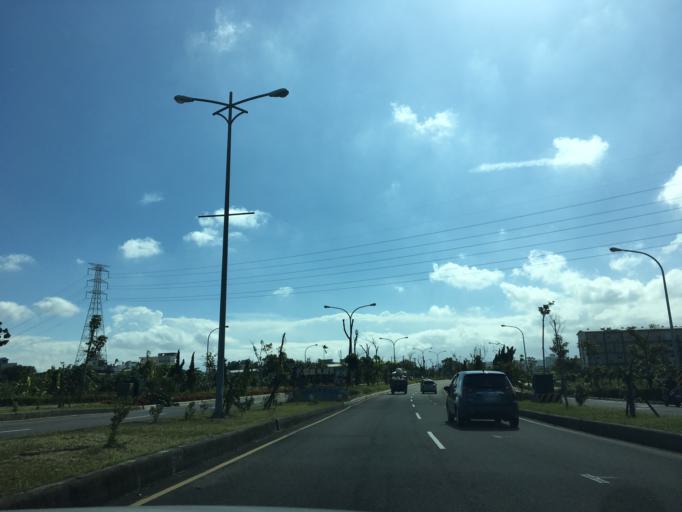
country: TW
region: Taiwan
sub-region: Hsinchu
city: Zhubei
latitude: 24.7935
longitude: 121.0216
